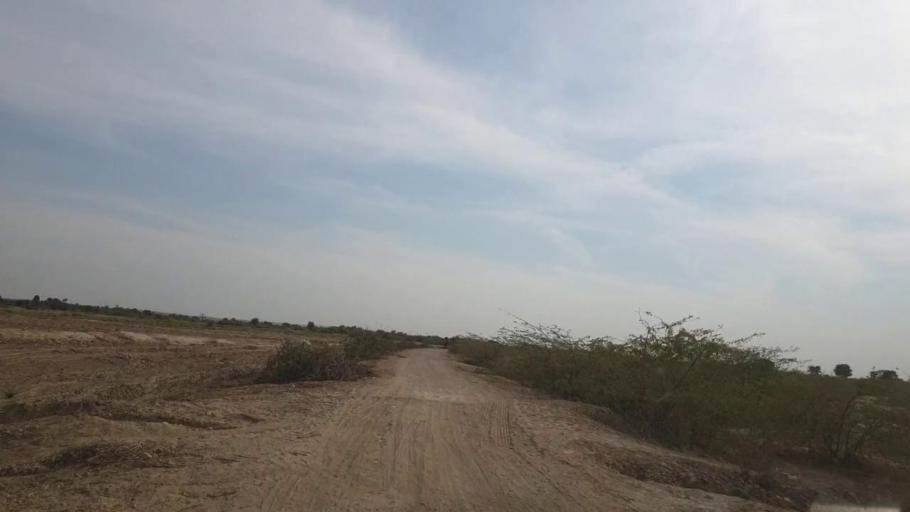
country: PK
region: Sindh
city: Nabisar
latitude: 25.0109
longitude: 69.5621
